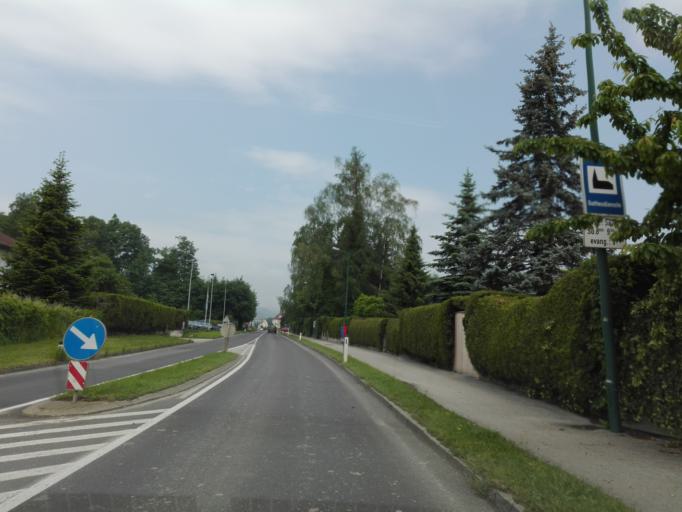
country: AT
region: Upper Austria
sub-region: Politischer Bezirk Urfahr-Umgebung
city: Feldkirchen an der Donau
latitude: 48.3029
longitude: 14.0296
